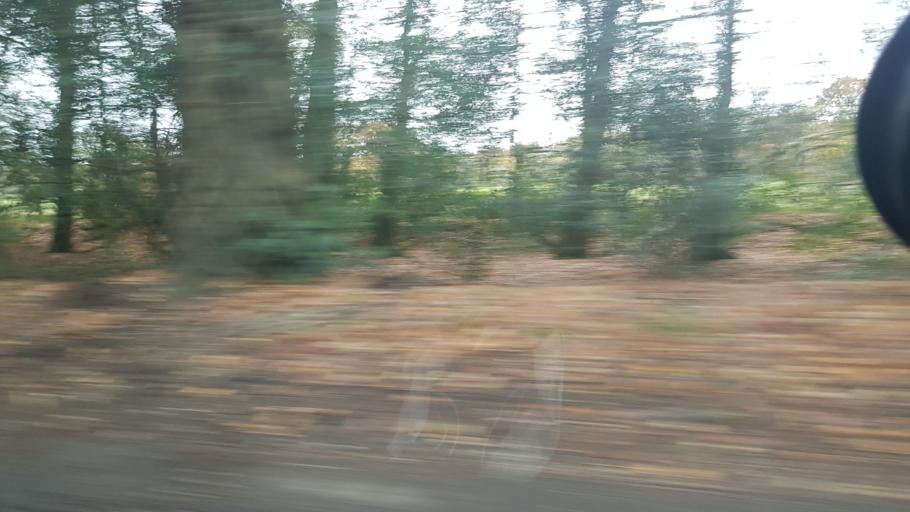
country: GB
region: England
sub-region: Hampshire
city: Eversley
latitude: 51.3517
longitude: -0.8879
